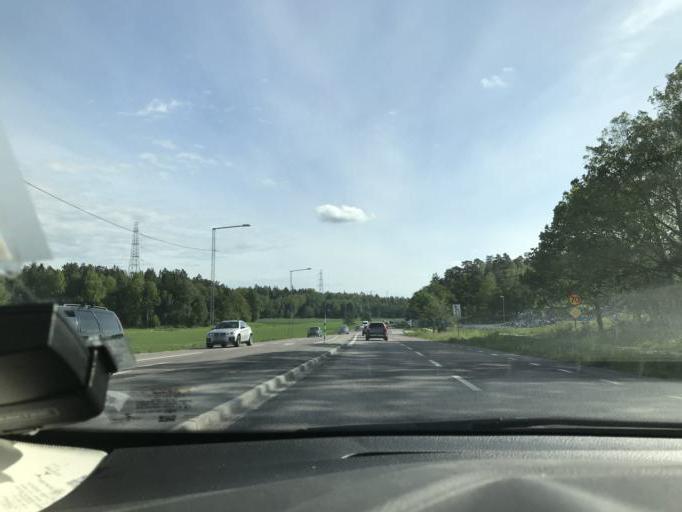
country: SE
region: Stockholm
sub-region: Botkyrka Kommun
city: Alby
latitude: 59.2281
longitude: 17.8403
